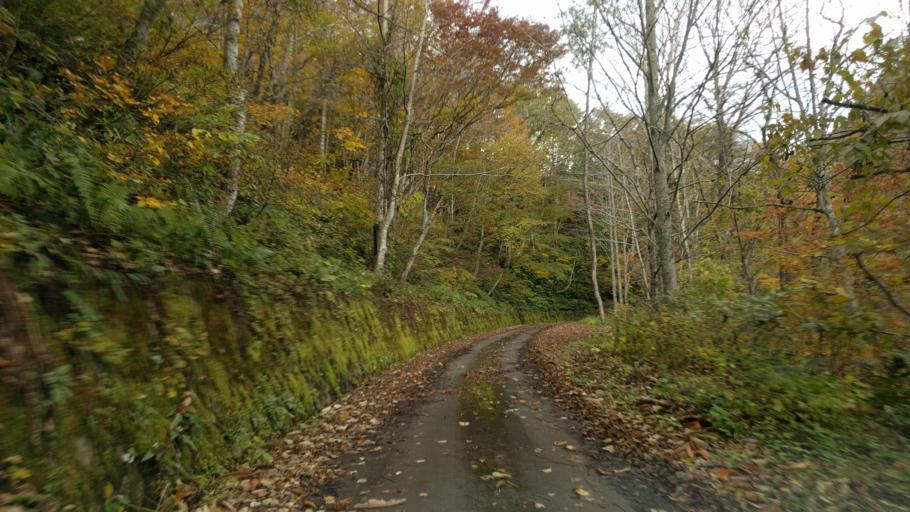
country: JP
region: Fukushima
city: Kitakata
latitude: 37.3895
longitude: 139.7152
